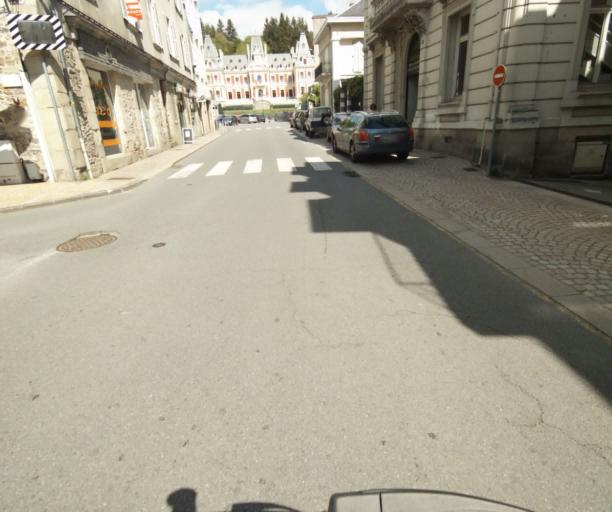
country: FR
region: Limousin
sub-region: Departement de la Correze
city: Tulle
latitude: 45.2696
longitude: 1.7692
